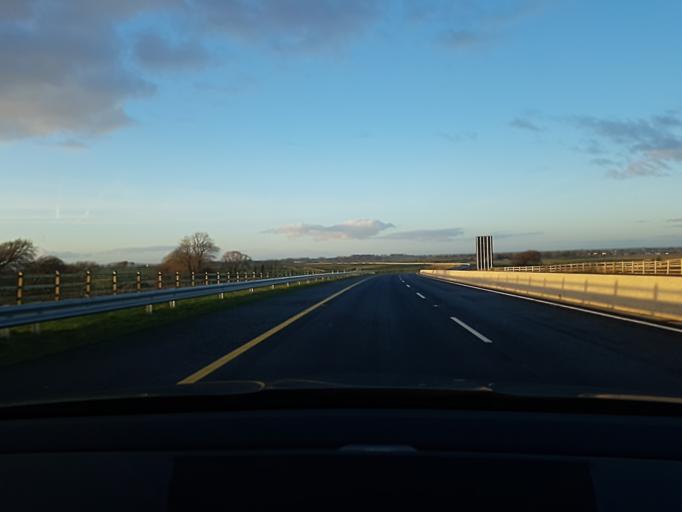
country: IE
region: Connaught
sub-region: County Galway
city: Tuam
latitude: 53.4141
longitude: -8.8286
